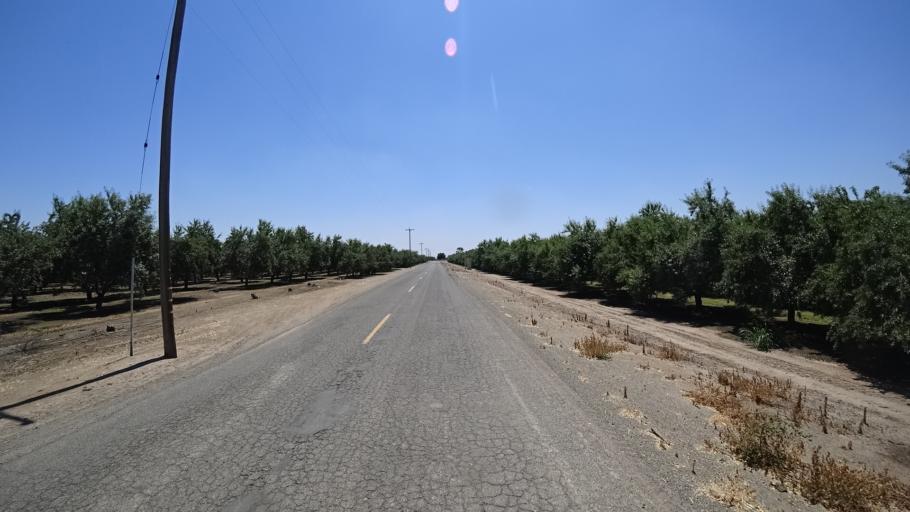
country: US
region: California
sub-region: Kings County
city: Lucerne
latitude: 36.4046
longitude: -119.6010
